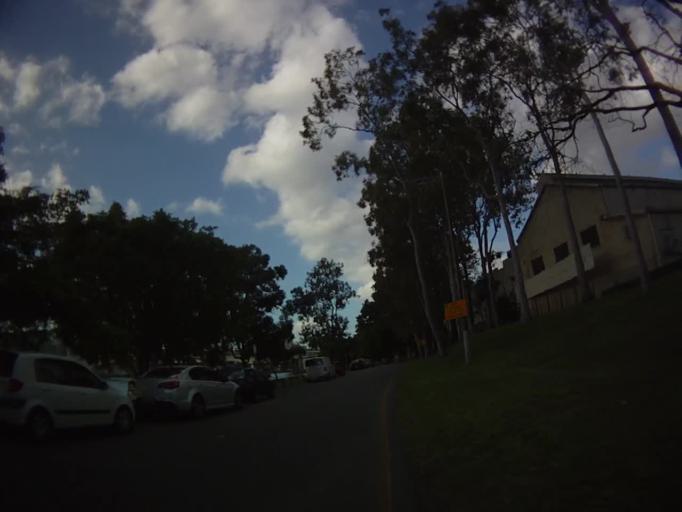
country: AU
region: Queensland
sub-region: Brisbane
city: Milton
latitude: -27.4719
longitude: 153.0110
